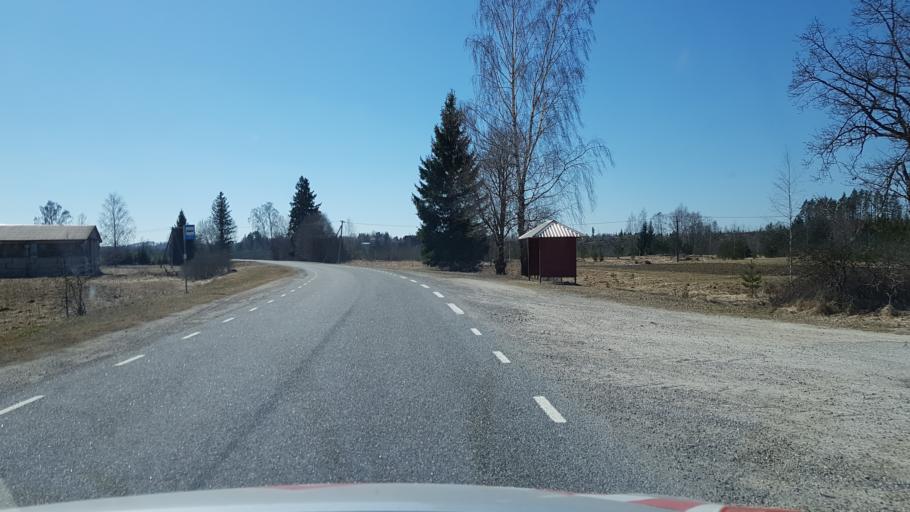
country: EE
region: Laeaene-Virumaa
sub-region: Rakke vald
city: Rakke
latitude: 58.9983
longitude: 26.2750
